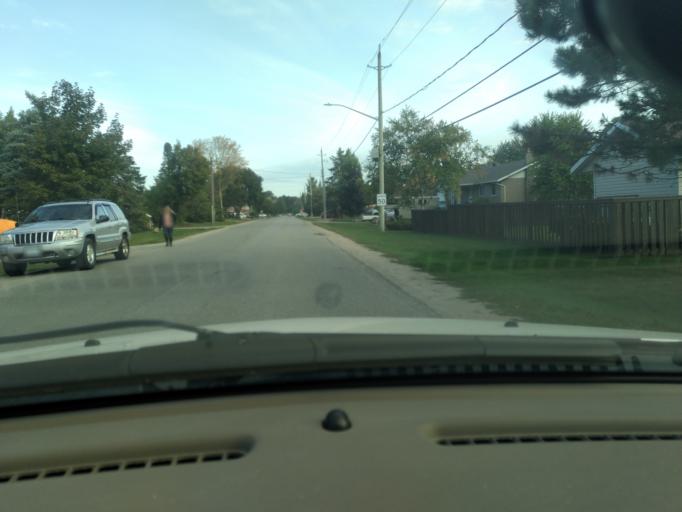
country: CA
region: Ontario
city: Innisfil
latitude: 44.3152
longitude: -79.5530
